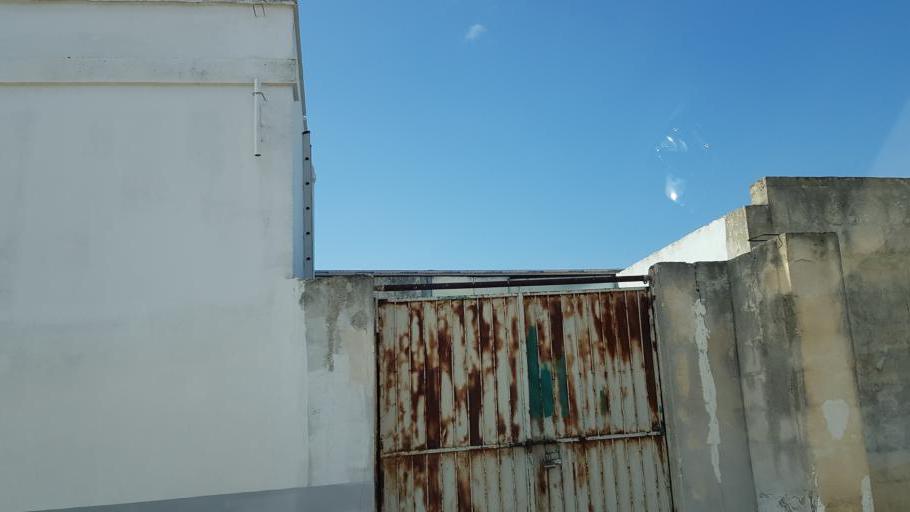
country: IT
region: Apulia
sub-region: Provincia di Brindisi
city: Materdomini
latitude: 40.6553
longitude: 17.9541
